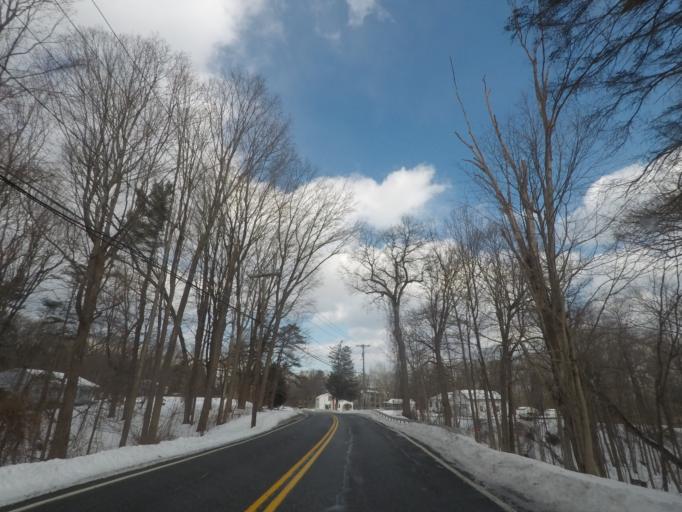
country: US
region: New York
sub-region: Albany County
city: Cohoes
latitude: 42.8183
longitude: -73.7447
